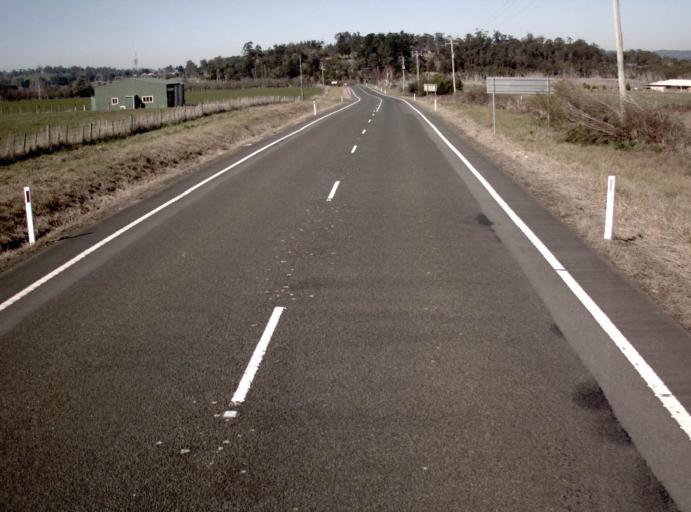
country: AU
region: Tasmania
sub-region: Launceston
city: Mayfield
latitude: -41.3116
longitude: 147.0520
